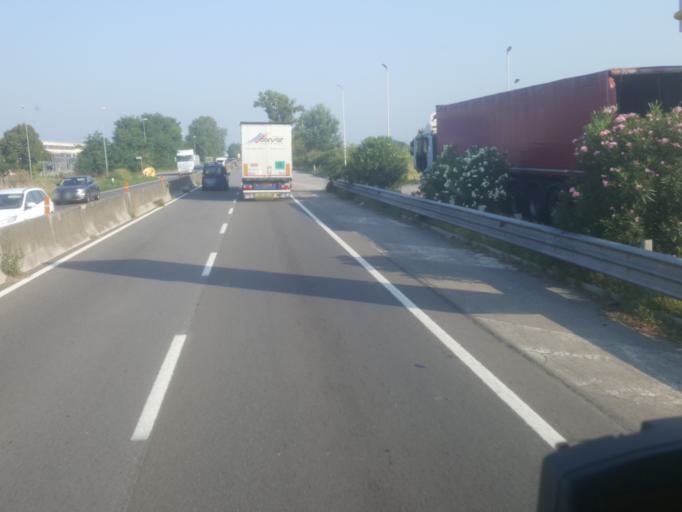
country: IT
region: Emilia-Romagna
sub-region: Provincia di Ravenna
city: Ravenna
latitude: 44.4148
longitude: 12.1698
